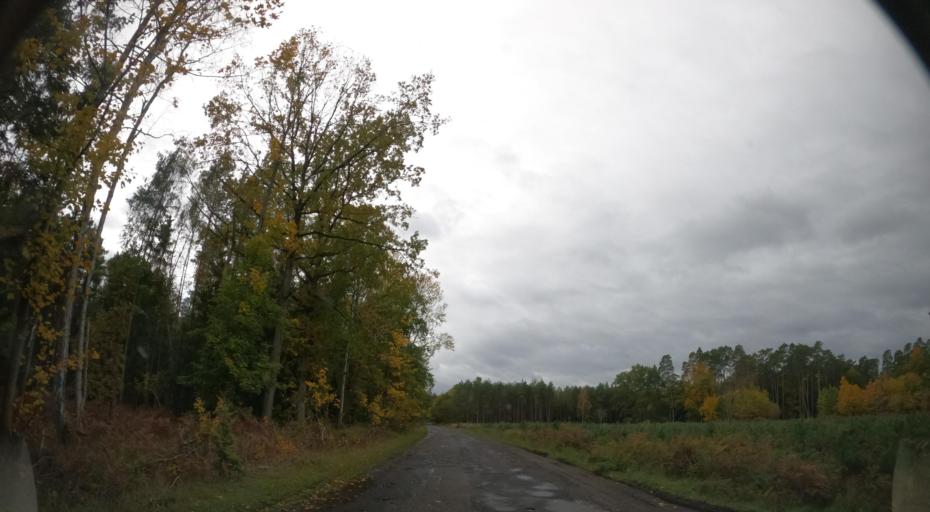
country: PL
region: West Pomeranian Voivodeship
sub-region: Powiat goleniowski
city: Stepnica
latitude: 53.6793
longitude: 14.6728
